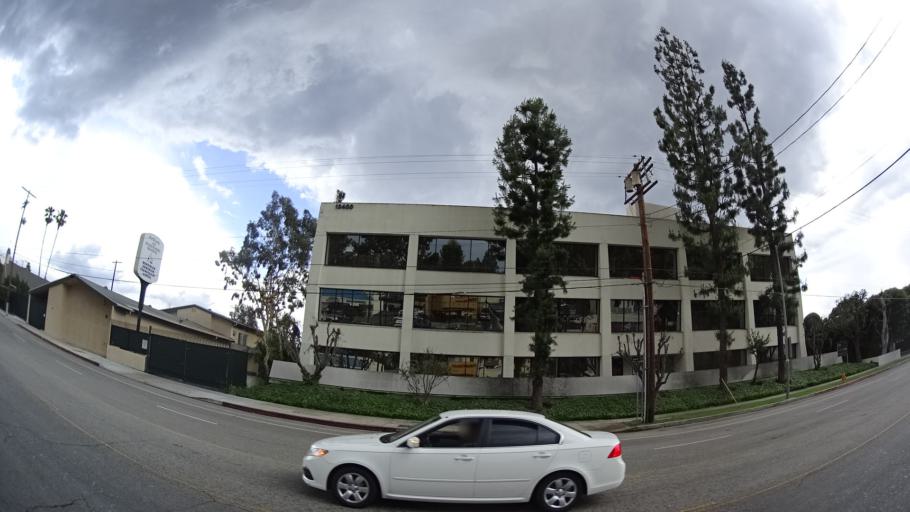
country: US
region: California
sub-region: Los Angeles County
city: Sherman Oaks
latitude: 34.1577
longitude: -118.4246
